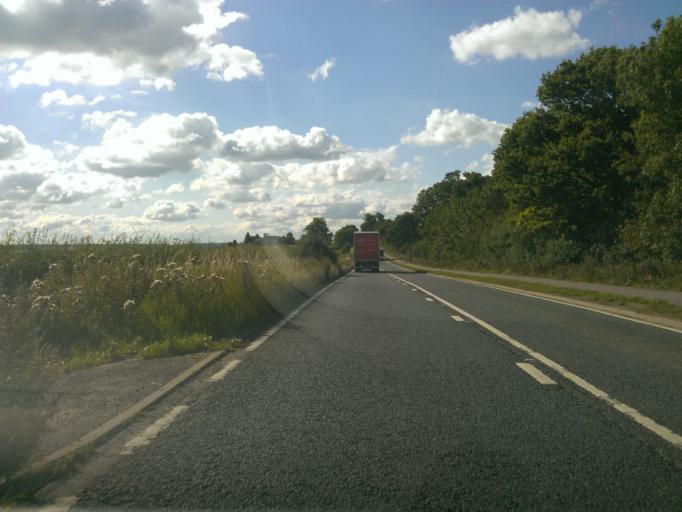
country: GB
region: England
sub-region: Warwickshire
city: Nuneaton
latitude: 52.5482
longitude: -1.4506
